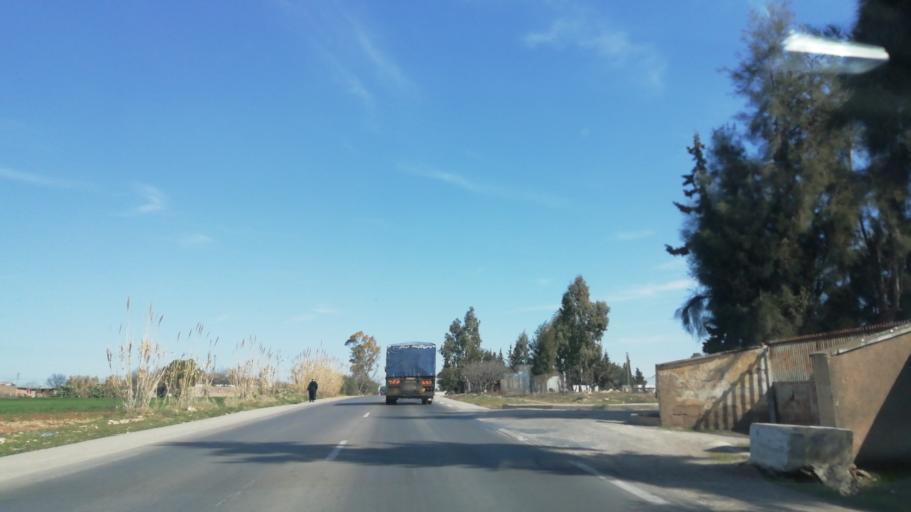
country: DZ
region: Mascara
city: Mascara
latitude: 35.4147
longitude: 0.3853
